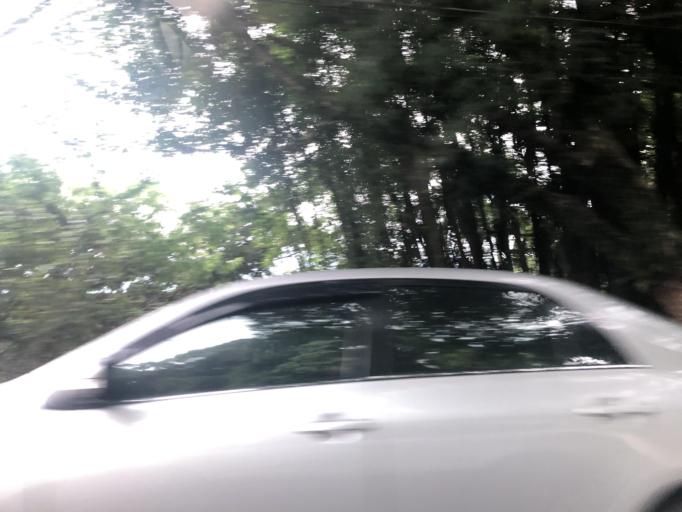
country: TW
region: Taiwan
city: Daxi
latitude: 24.8864
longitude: 121.4190
